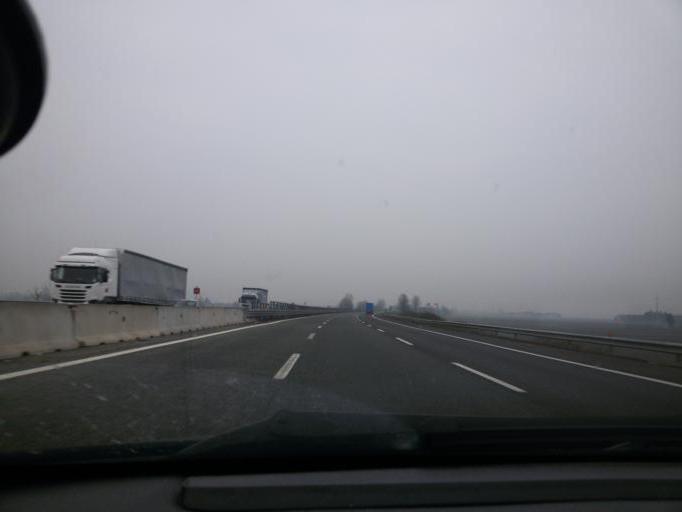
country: IT
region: Piedmont
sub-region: Provincia di Alessandria
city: Villanova Monferrato
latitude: 45.1540
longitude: 8.4839
